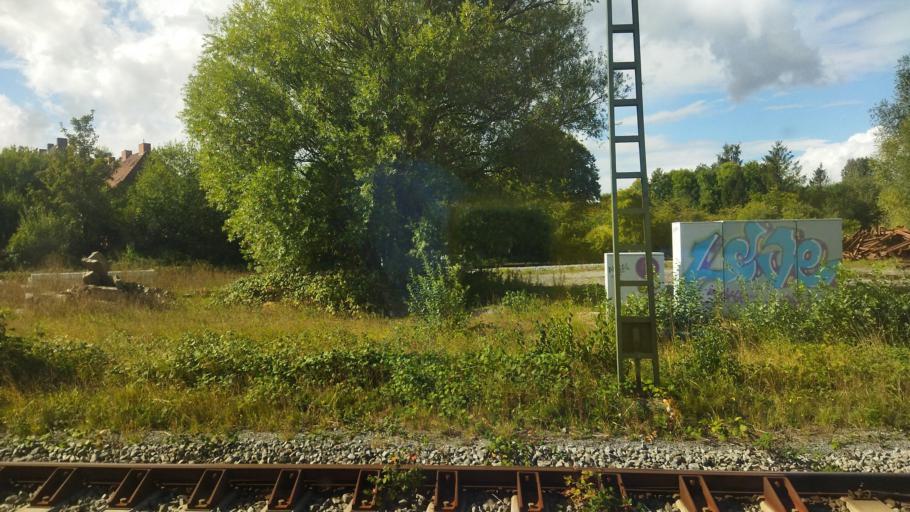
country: DE
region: Lower Saxony
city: Emden
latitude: 53.3660
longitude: 7.1953
